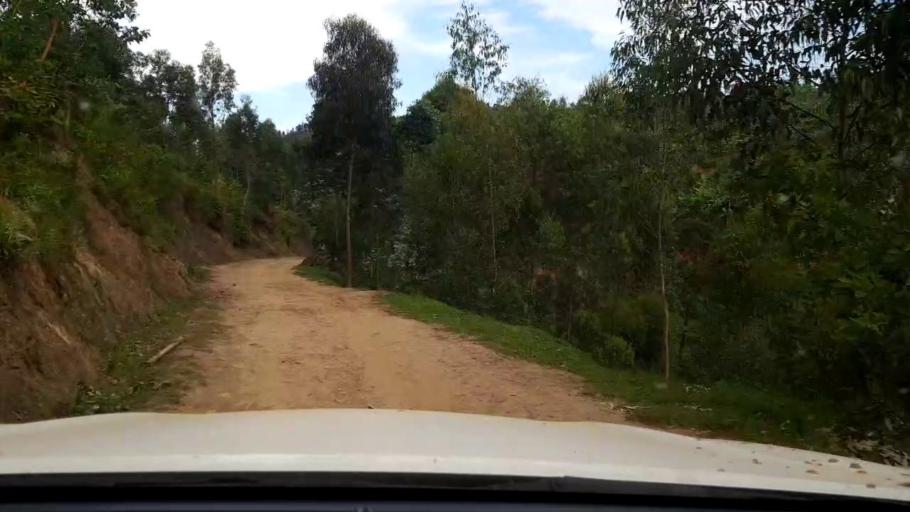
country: RW
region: Western Province
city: Kibuye
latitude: -2.0025
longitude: 29.3716
